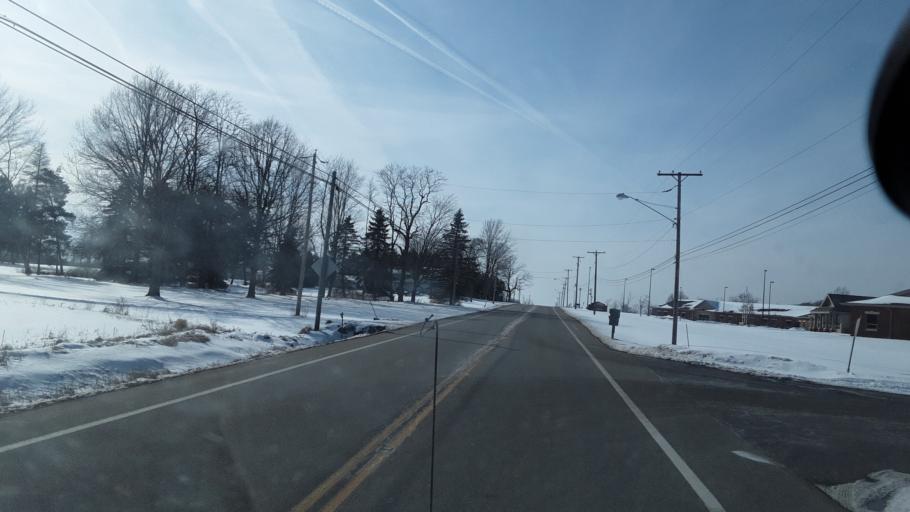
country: US
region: Ohio
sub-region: Mahoning County
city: Craig Beach
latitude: 41.0248
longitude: -80.9105
